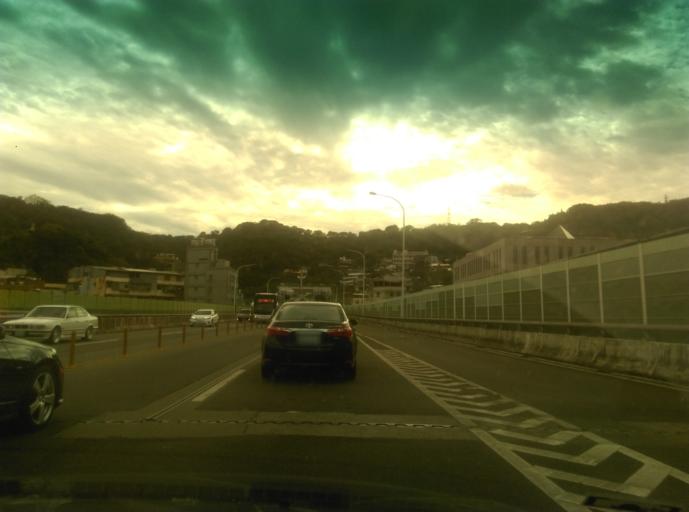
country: TW
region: Taiwan
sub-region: Keelung
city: Keelung
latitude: 25.1261
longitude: 121.7377
